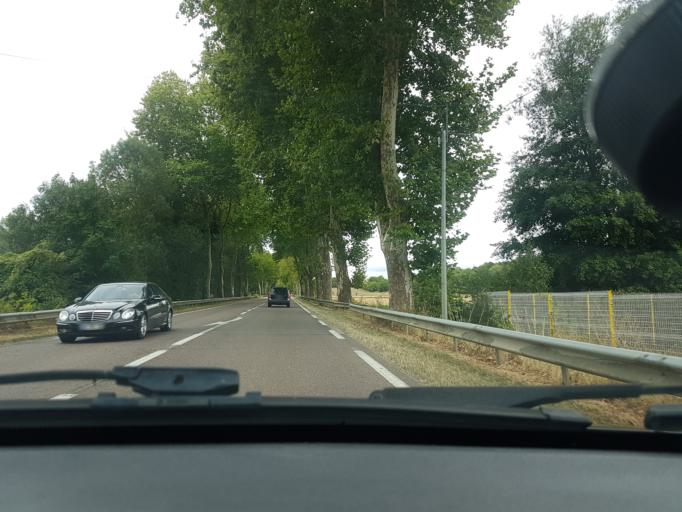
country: FR
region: Bourgogne
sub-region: Departement de l'Yonne
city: Champs-sur-Yonne
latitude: 47.7187
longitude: 3.6139
